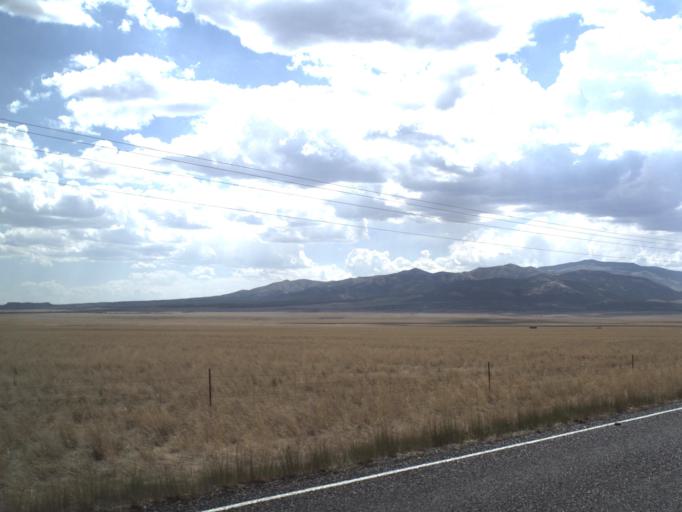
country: US
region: Idaho
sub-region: Power County
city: American Falls
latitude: 41.9661
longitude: -113.0684
